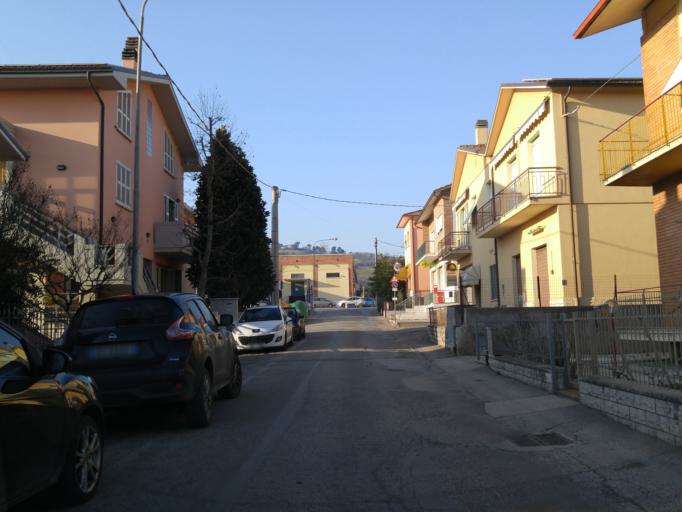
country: IT
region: The Marches
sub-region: Provincia di Pesaro e Urbino
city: Cuccurano
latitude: 43.8016
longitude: 12.9735
